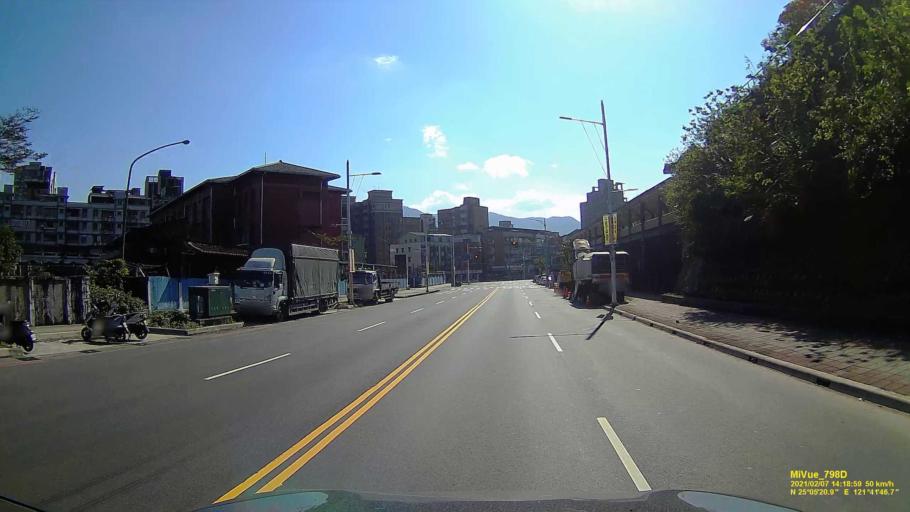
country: TW
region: Taiwan
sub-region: Keelung
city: Keelung
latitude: 25.0890
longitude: 121.6962
